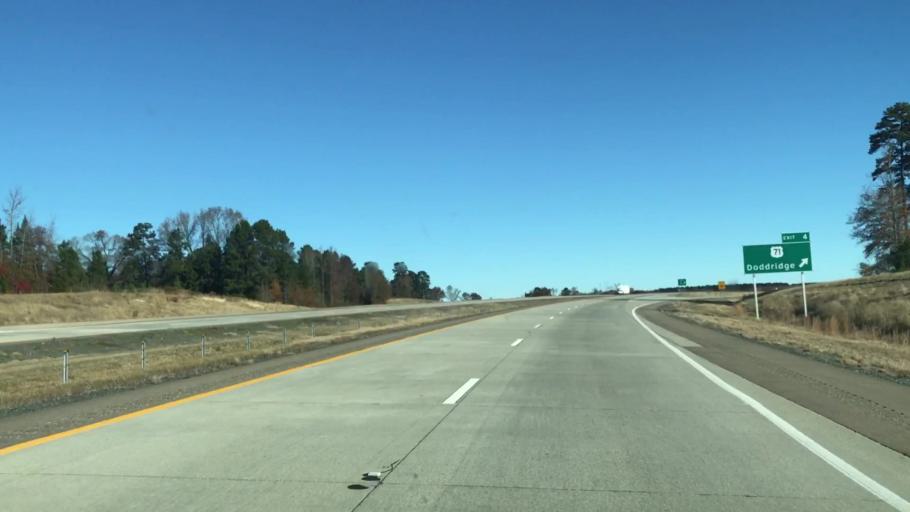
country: US
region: Louisiana
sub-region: Caddo Parish
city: Vivian
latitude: 33.0744
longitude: -93.9045
